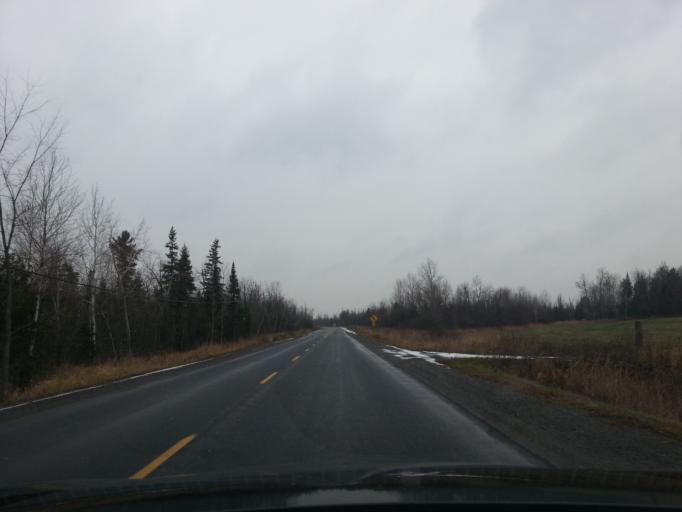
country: CA
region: Ontario
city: Carleton Place
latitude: 45.1075
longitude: -76.0378
